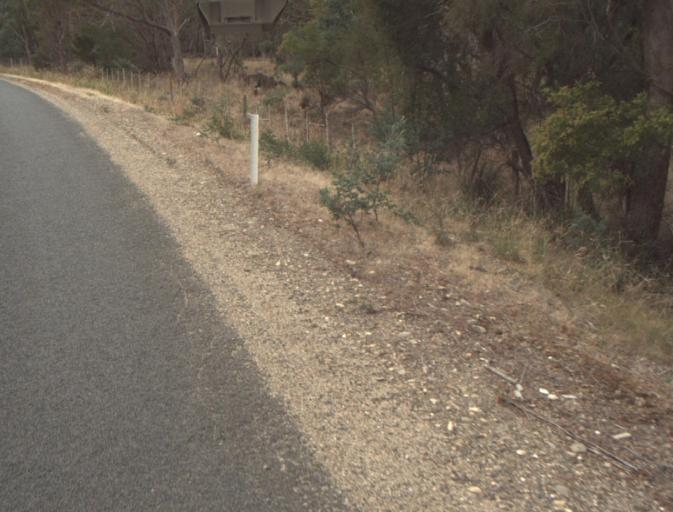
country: AU
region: Tasmania
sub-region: Northern Midlands
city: Evandale
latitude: -41.5137
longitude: 147.3381
